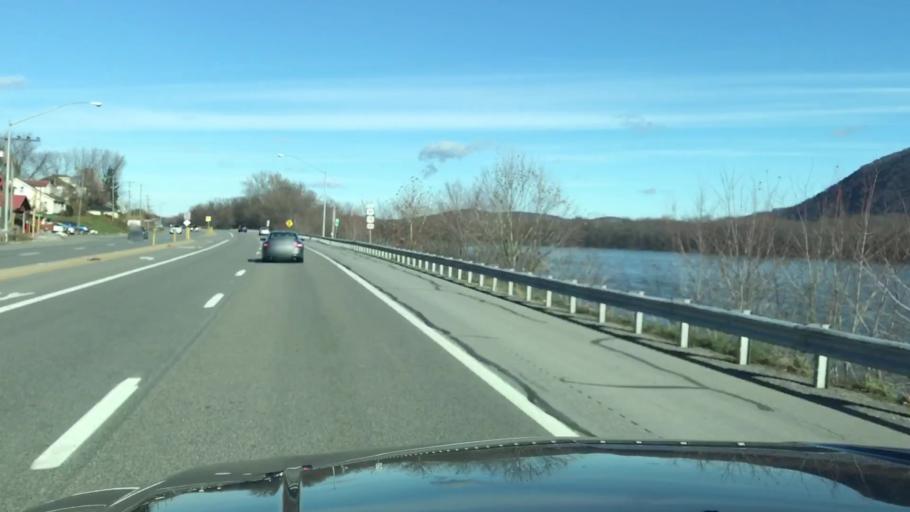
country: US
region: Pennsylvania
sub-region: Snyder County
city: Selinsgrove
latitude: 40.7276
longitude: -76.8556
